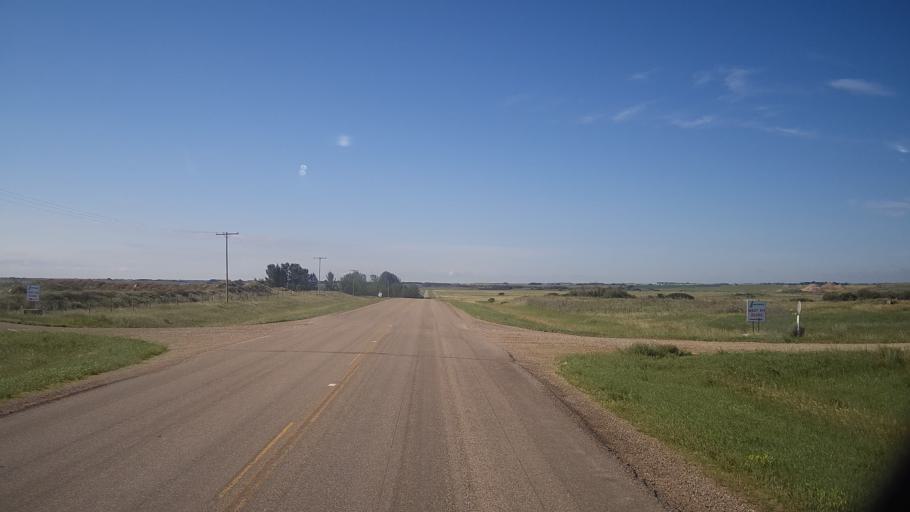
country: CA
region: Saskatchewan
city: Watrous
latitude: 51.7247
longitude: -105.3574
